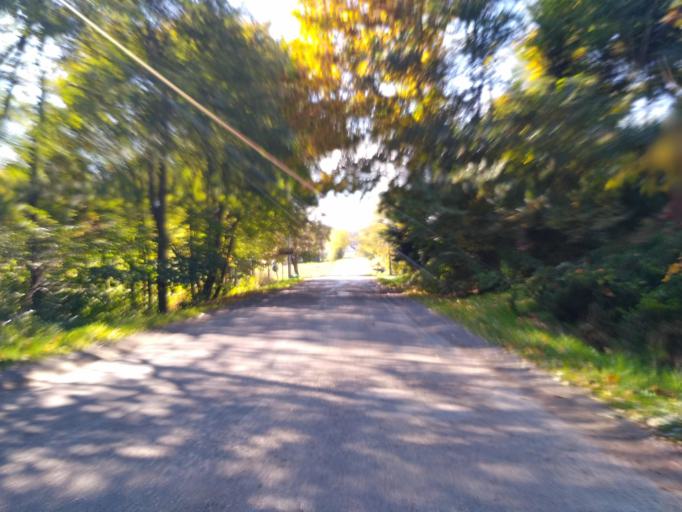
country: PL
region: Subcarpathian Voivodeship
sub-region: Powiat debicki
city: Slotowa
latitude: 49.9411
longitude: 21.2822
